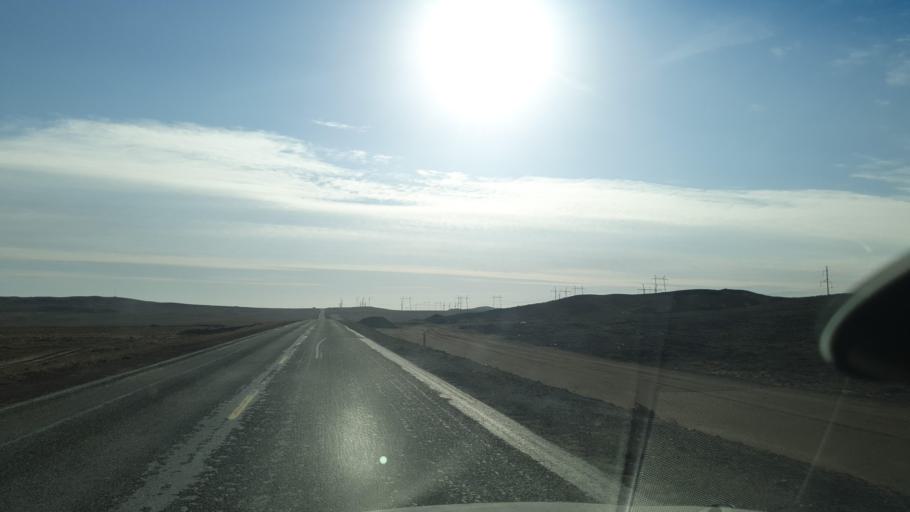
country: KZ
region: Zhambyl
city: Mynaral
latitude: 45.6786
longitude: 73.4010
